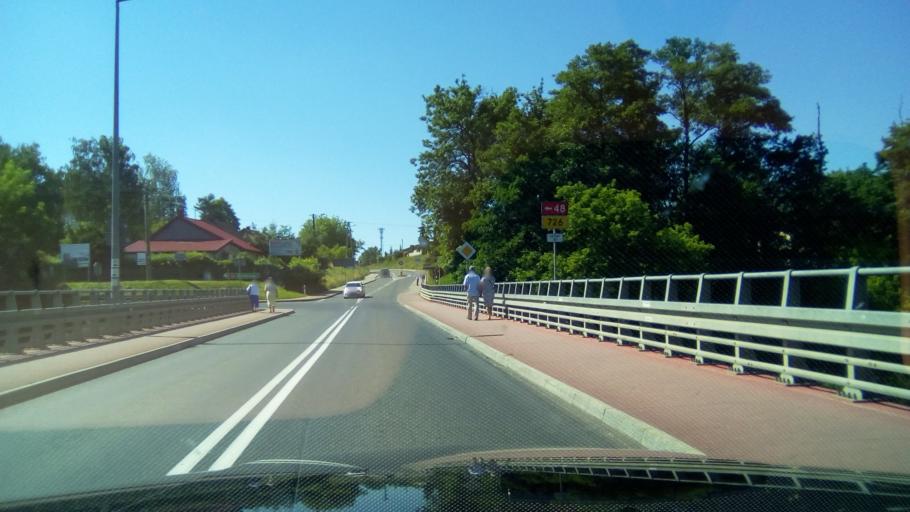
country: PL
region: Lodz Voivodeship
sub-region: Powiat tomaszowski
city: Inowlodz
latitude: 51.5208
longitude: 20.2229
